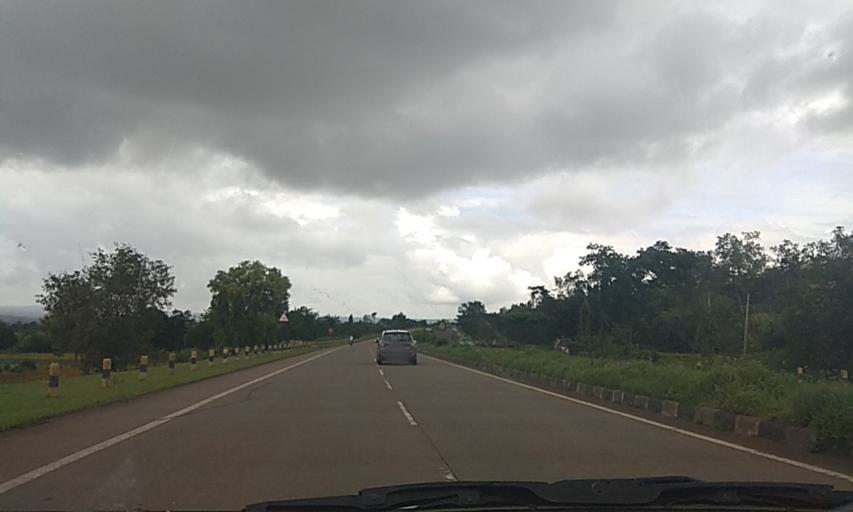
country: IN
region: Karnataka
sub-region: Belgaum
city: Sankeshwar
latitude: 16.2806
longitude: 74.4475
